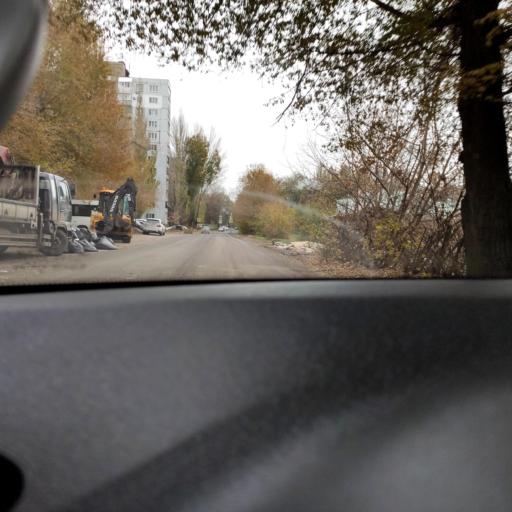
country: RU
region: Samara
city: Samara
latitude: 53.2360
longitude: 50.2452
